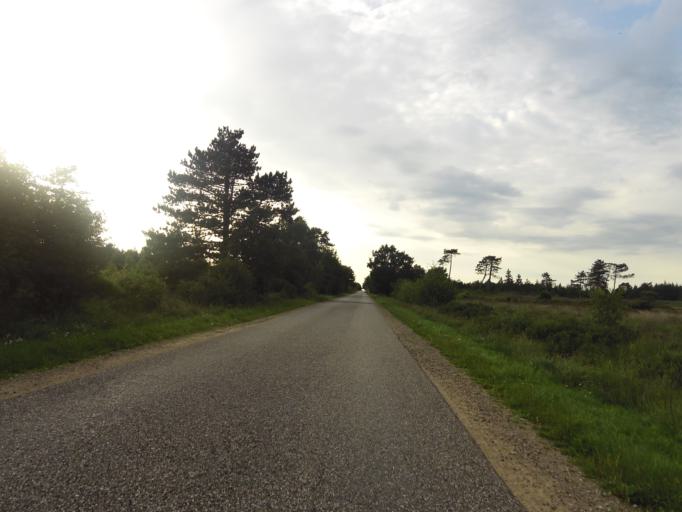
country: DK
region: South Denmark
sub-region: Tonder Kommune
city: Logumkloster
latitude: 55.1651
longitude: 8.9231
